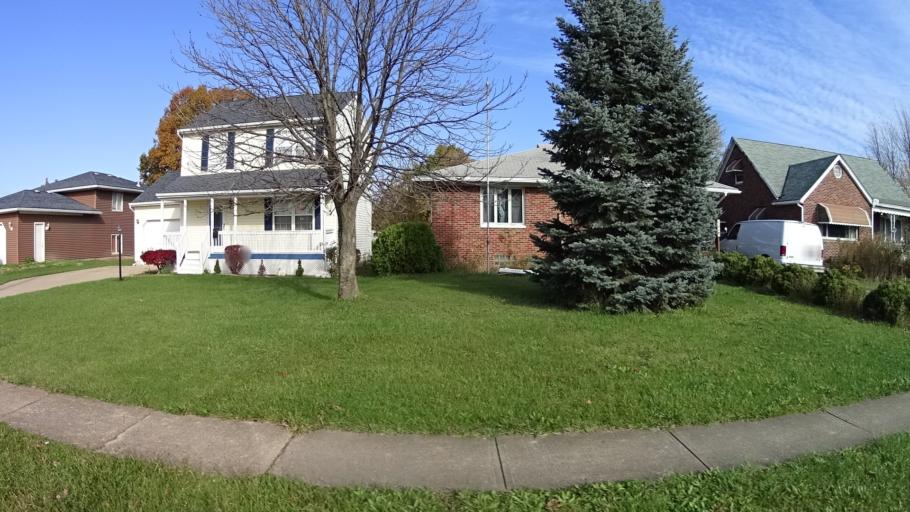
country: US
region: Ohio
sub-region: Lorain County
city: Lorain
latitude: 41.4376
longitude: -82.1448
